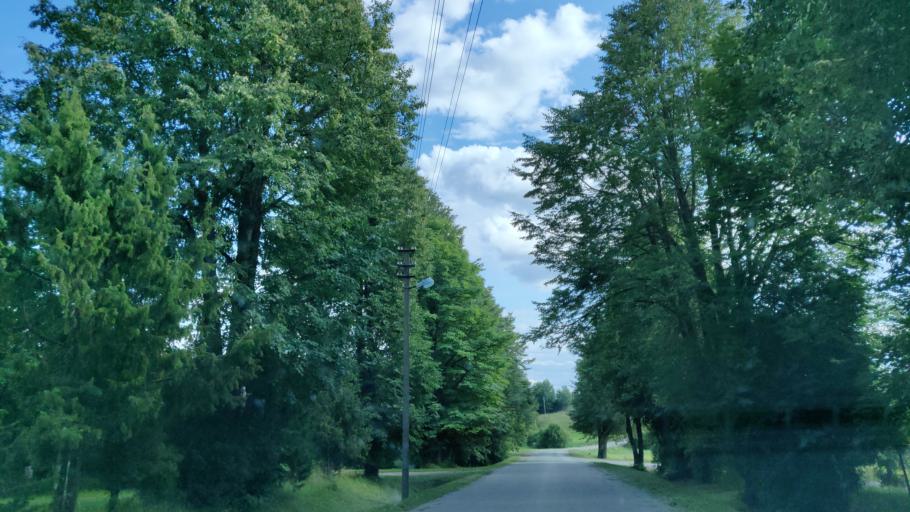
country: LT
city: Varniai
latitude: 55.5964
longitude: 22.3107
